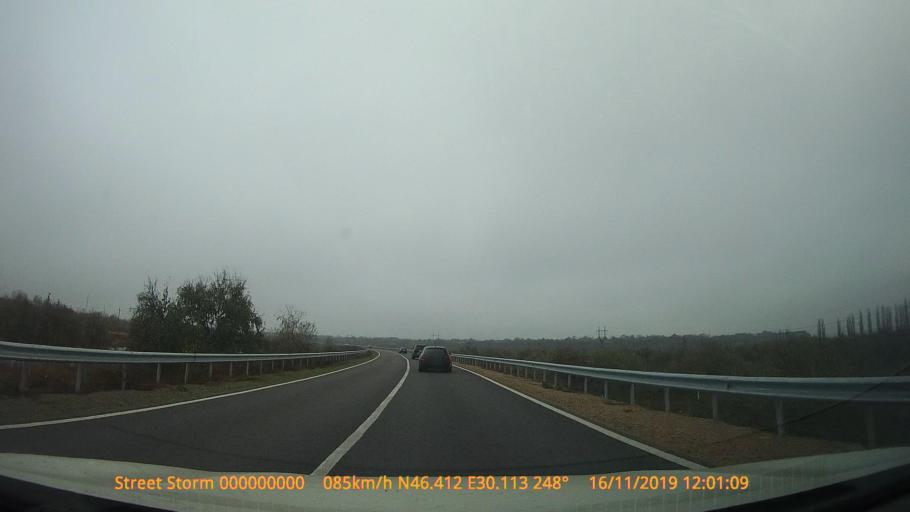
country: UA
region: Odessa
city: Bilyayivka
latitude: 46.4112
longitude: 30.1104
